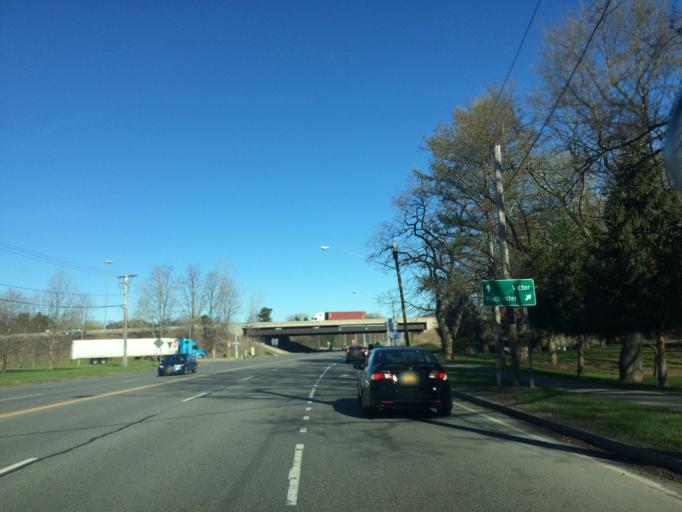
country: US
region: New York
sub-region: Monroe County
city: East Rochester
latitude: 43.1099
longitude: -77.5051
